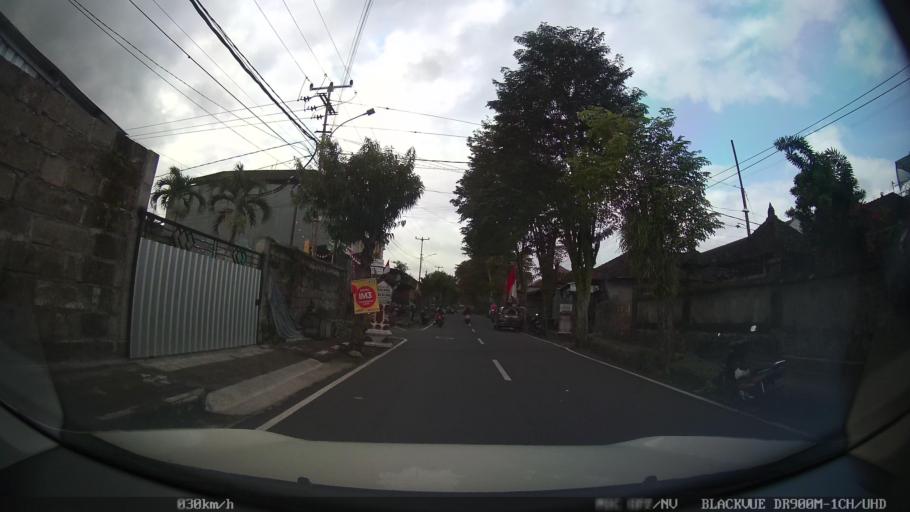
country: ID
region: Bali
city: Banjar Jambe Baleran
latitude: -8.5367
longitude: 115.1229
